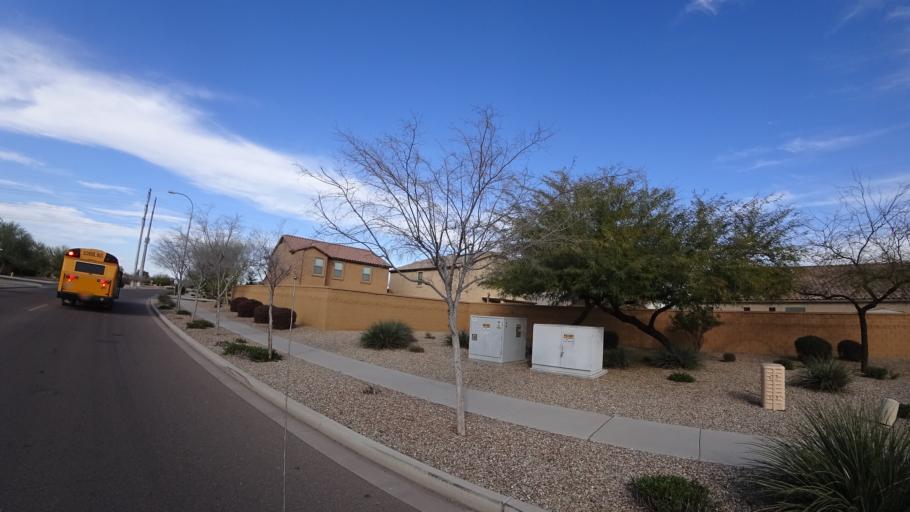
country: US
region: Arizona
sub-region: Maricopa County
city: Tolleson
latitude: 33.4122
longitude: -112.2807
